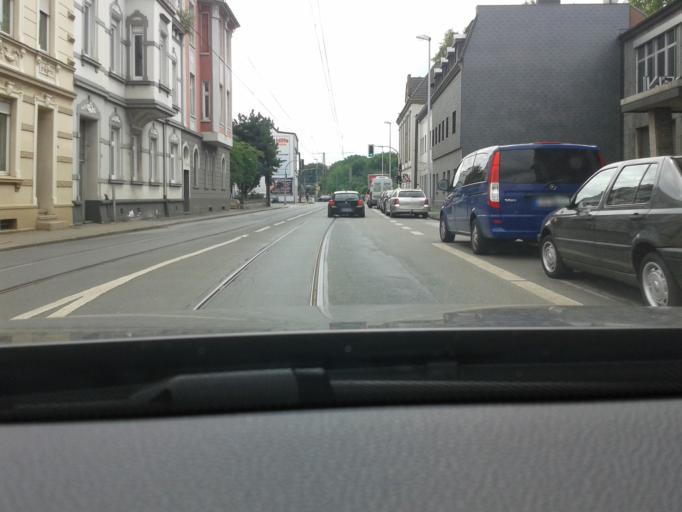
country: DE
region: North Rhine-Westphalia
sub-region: Regierungsbezirk Dusseldorf
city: Muelheim (Ruhr)
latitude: 51.4463
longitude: 6.8652
